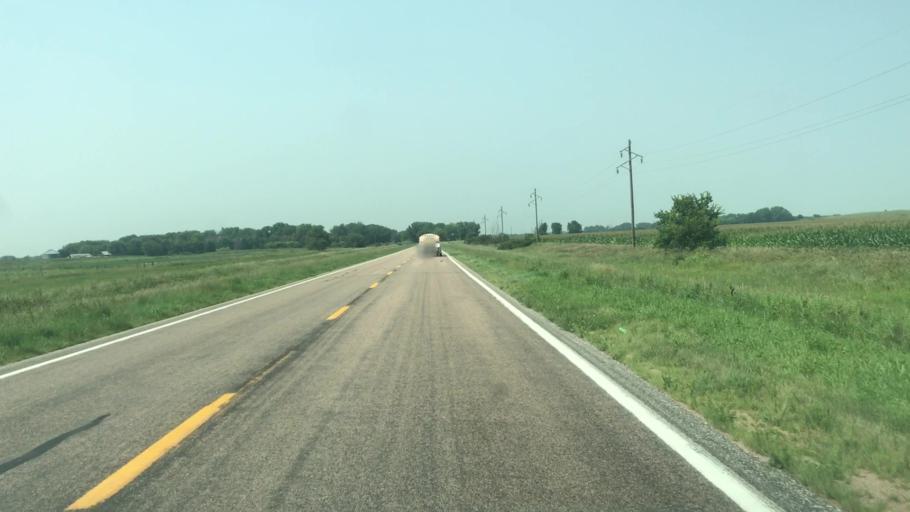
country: US
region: Nebraska
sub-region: Sherman County
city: Loup City
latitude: 41.2296
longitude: -98.9338
